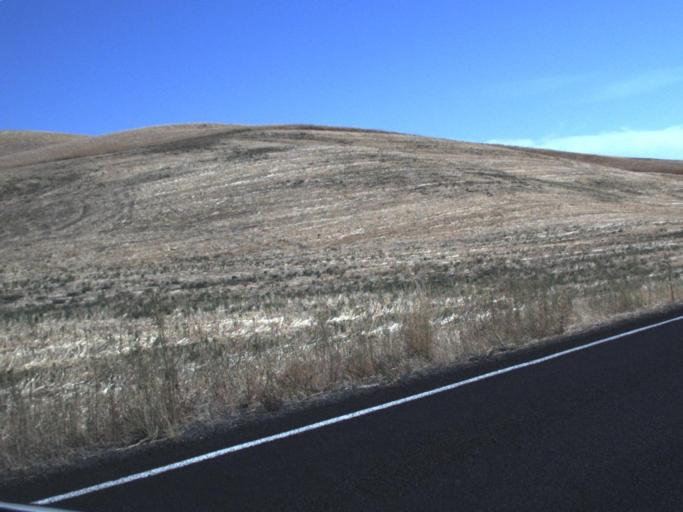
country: US
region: Washington
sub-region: Walla Walla County
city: Walla Walla
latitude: 46.2106
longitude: -118.3901
